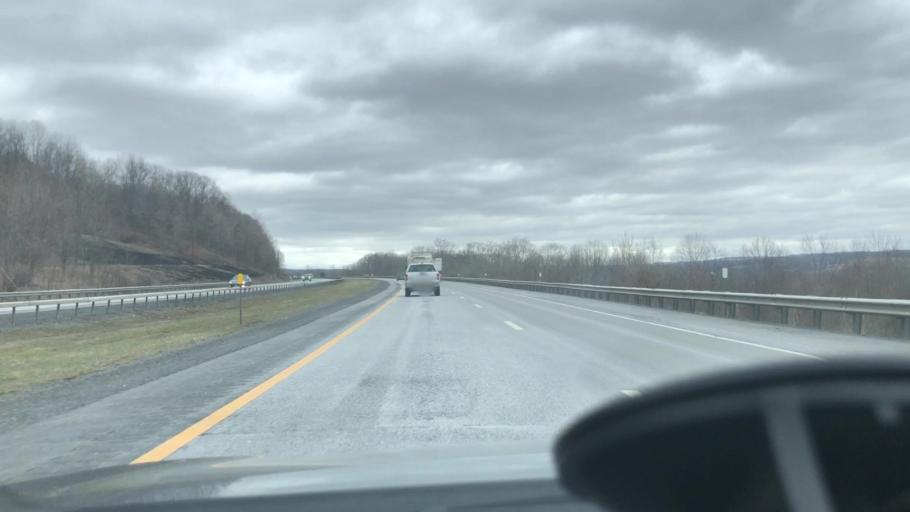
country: US
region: New York
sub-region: Herkimer County
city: Ilion
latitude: 43.0322
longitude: -75.0447
